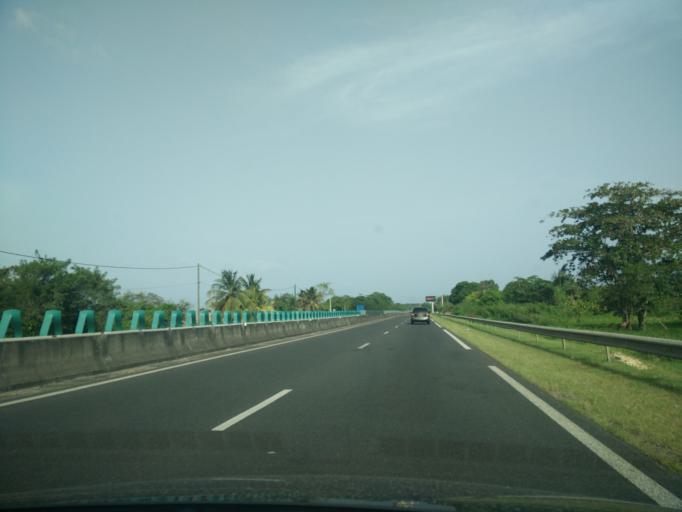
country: GP
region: Guadeloupe
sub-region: Guadeloupe
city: Petit-Bourg
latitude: 16.1790
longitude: -61.5962
